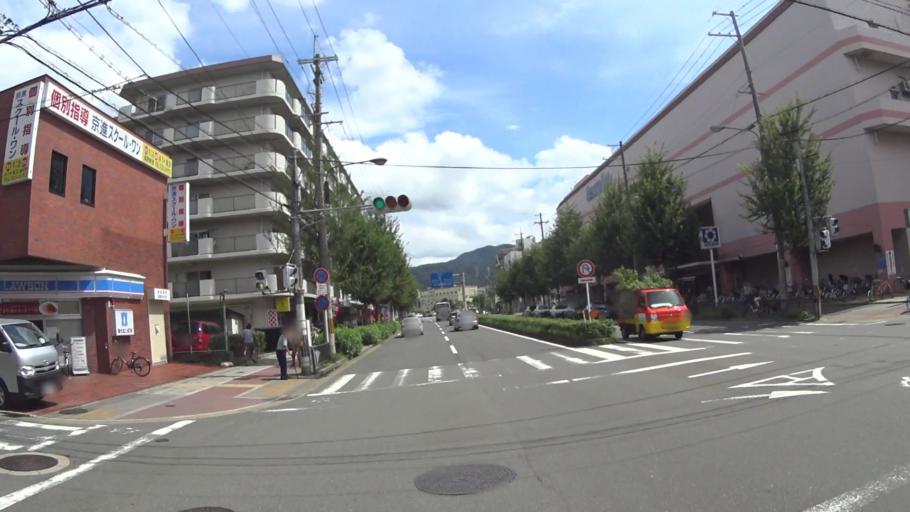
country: JP
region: Kyoto
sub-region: Kyoto-shi
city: Kamigyo-ku
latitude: 35.0419
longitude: 135.7806
